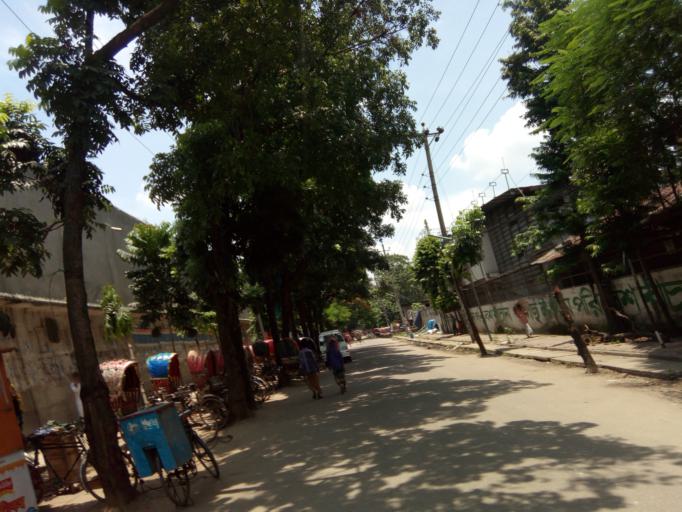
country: BD
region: Dhaka
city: Paltan
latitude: 23.7632
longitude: 90.4020
